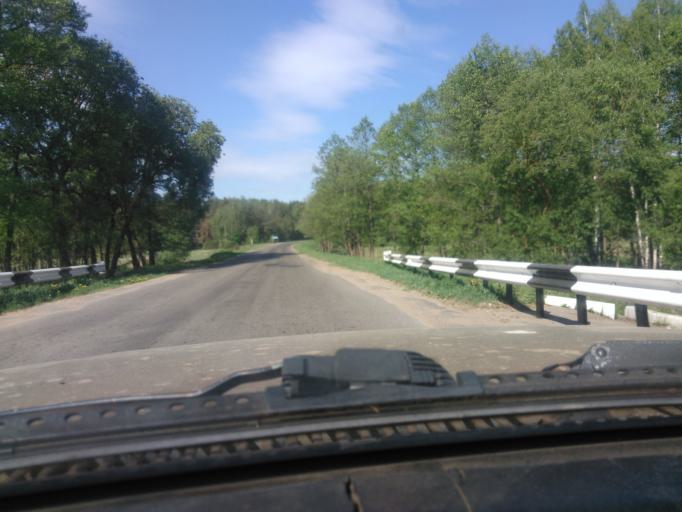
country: BY
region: Mogilev
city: Myazhysyatki
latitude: 53.8119
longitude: 30.1186
